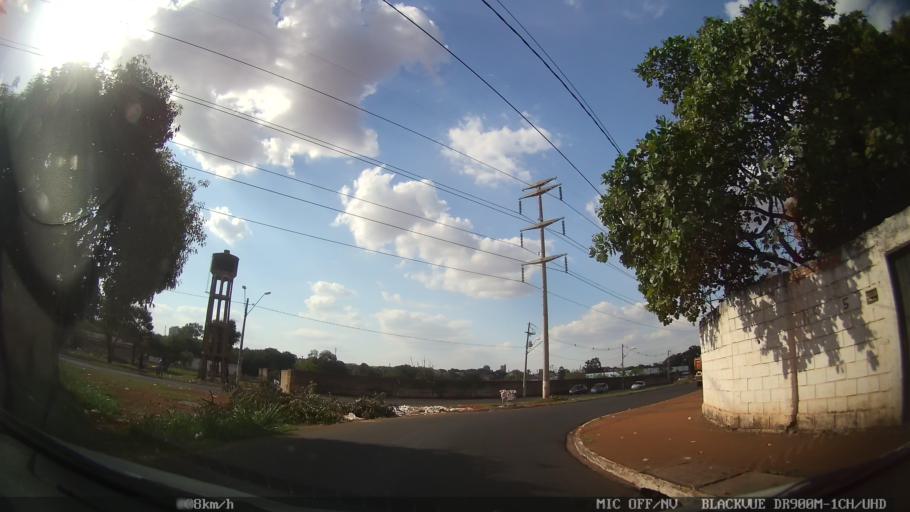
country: BR
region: Sao Paulo
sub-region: Ribeirao Preto
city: Ribeirao Preto
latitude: -21.1797
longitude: -47.8258
